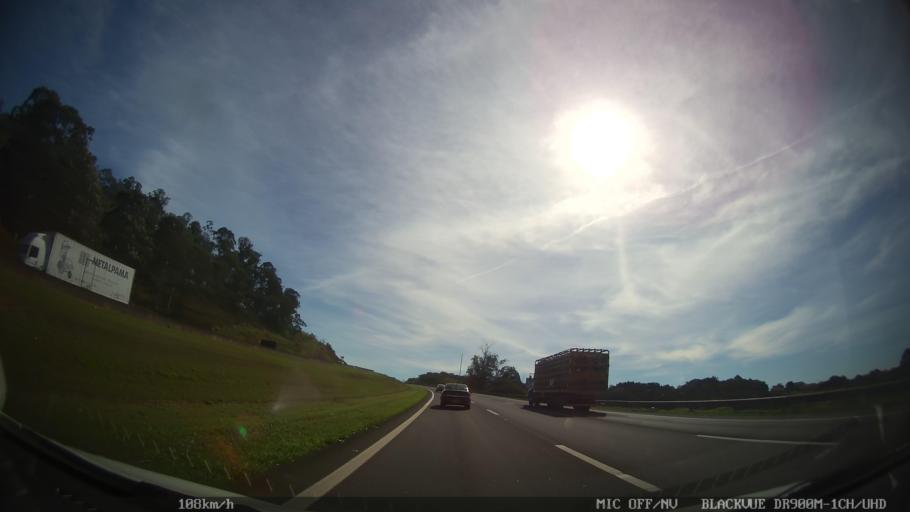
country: BR
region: Sao Paulo
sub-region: Araras
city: Araras
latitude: -22.3337
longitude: -47.3891
